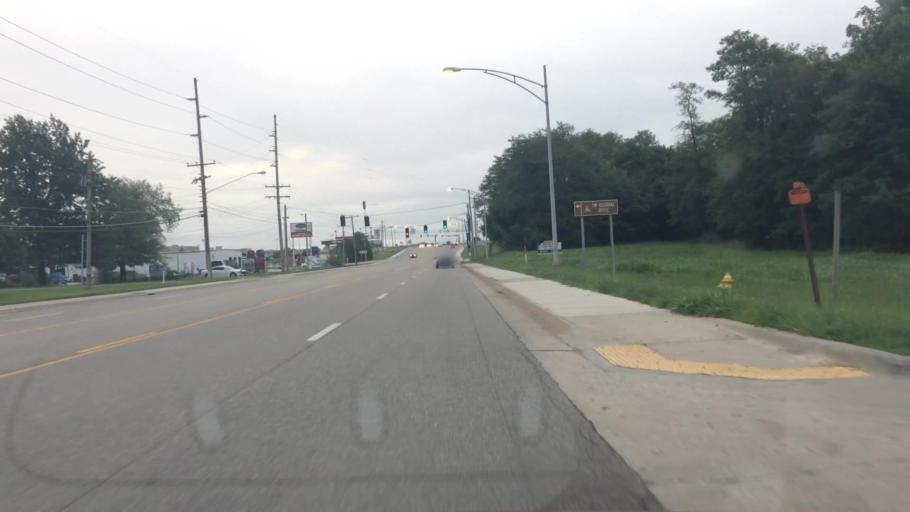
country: US
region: Missouri
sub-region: Greene County
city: Springfield
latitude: 37.2391
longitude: -93.2329
